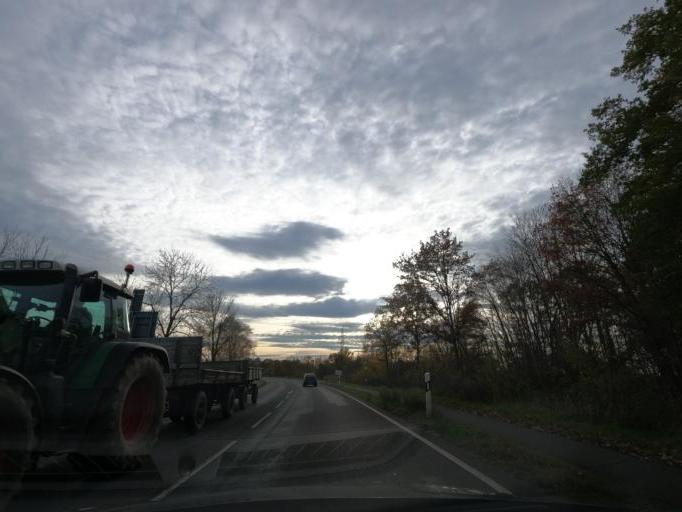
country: DE
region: Lower Saxony
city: Cremlingen
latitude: 52.2969
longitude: 10.5975
